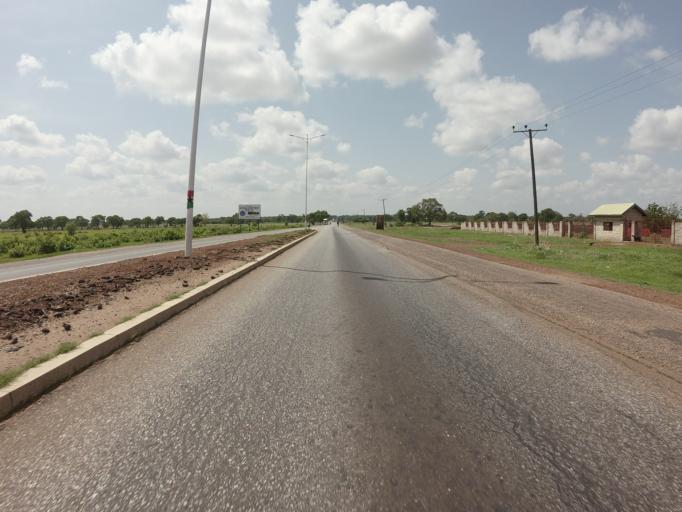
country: GH
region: Northern
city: Savelugu
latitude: 9.5555
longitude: -0.8370
